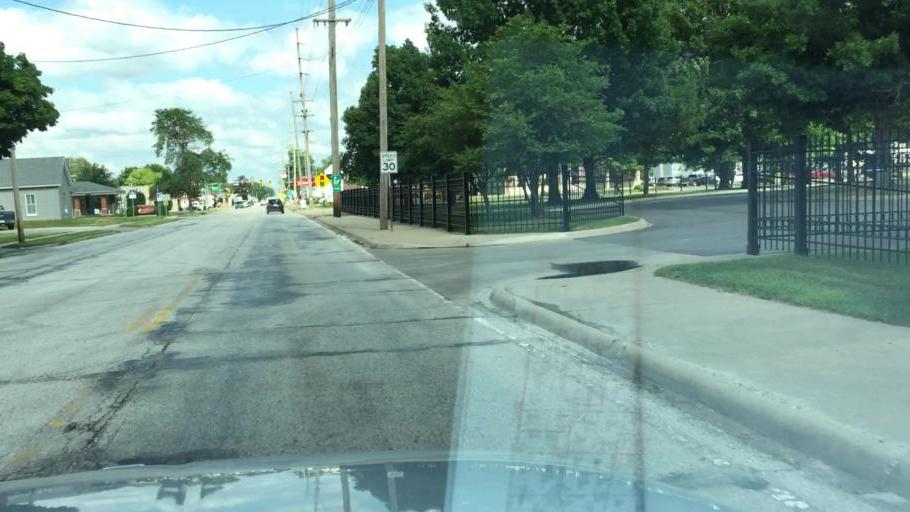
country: US
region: Illinois
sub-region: Hancock County
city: Carthage
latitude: 40.4162
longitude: -91.1392
